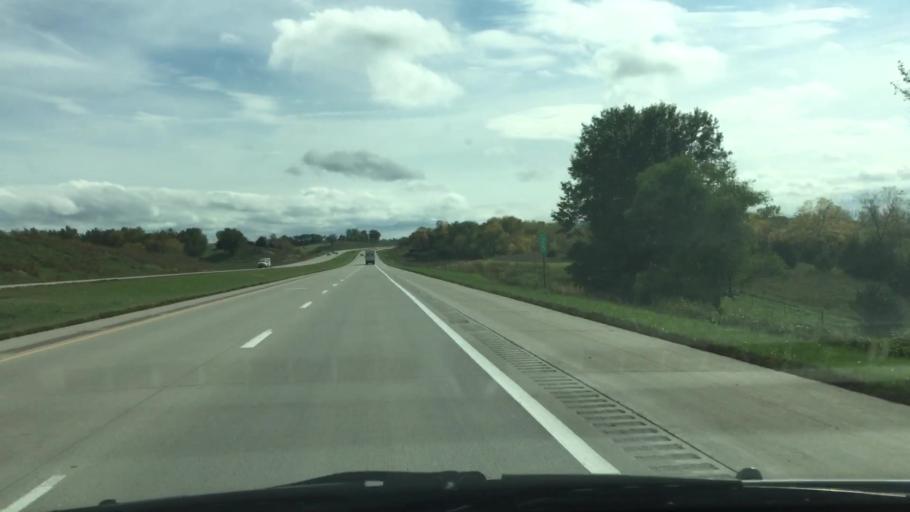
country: US
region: Iowa
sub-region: Clarke County
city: Osceola
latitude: 40.9084
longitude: -93.7983
